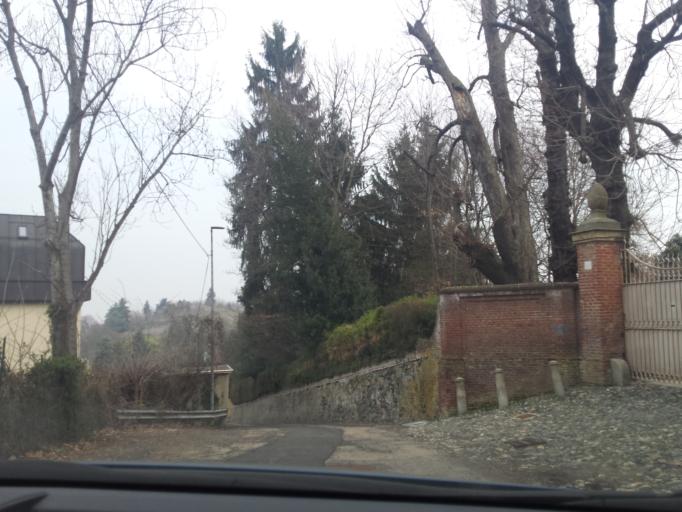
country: IT
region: Piedmont
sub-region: Provincia di Torino
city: Turin
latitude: 45.0617
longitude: 7.7300
